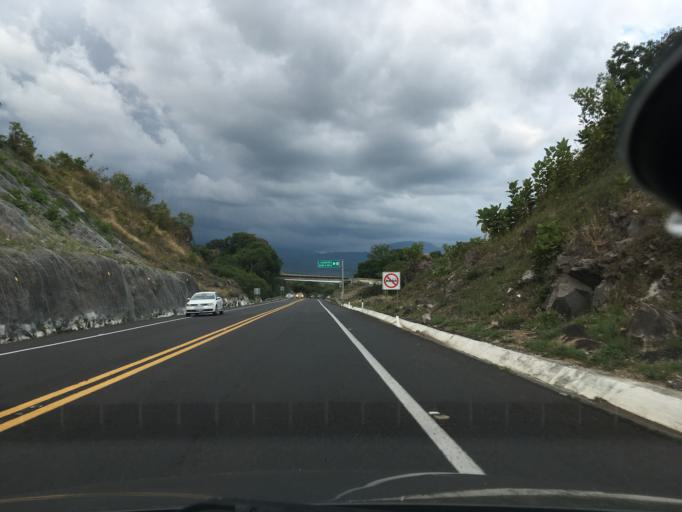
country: MX
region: Michoacan
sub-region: Ziracuaretiro
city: Patuan
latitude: 19.4165
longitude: -101.9480
